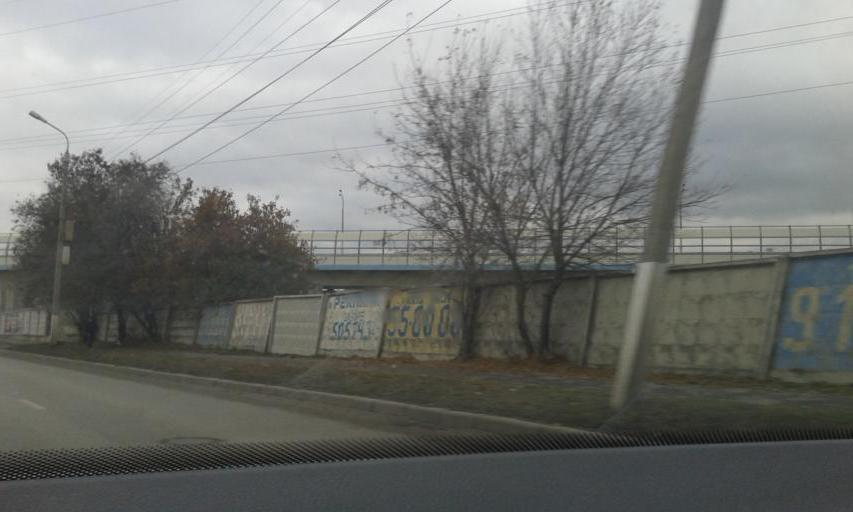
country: RU
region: Volgograd
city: Volgograd
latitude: 48.7323
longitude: 44.5276
